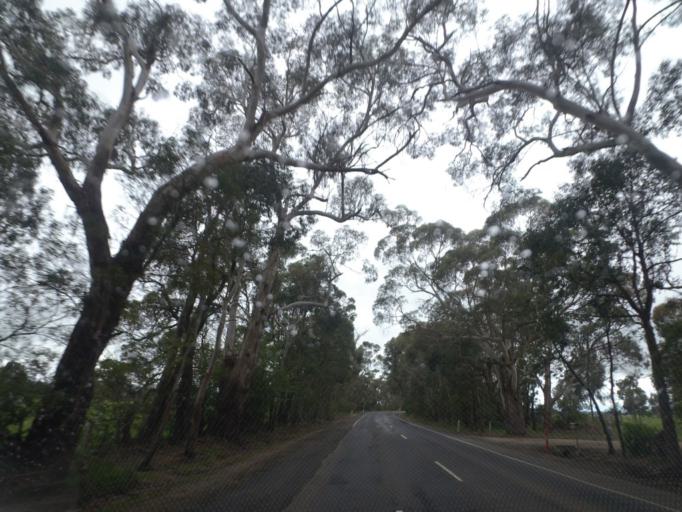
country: AU
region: Victoria
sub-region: Hume
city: Sunbury
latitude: -37.3443
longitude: 144.6898
